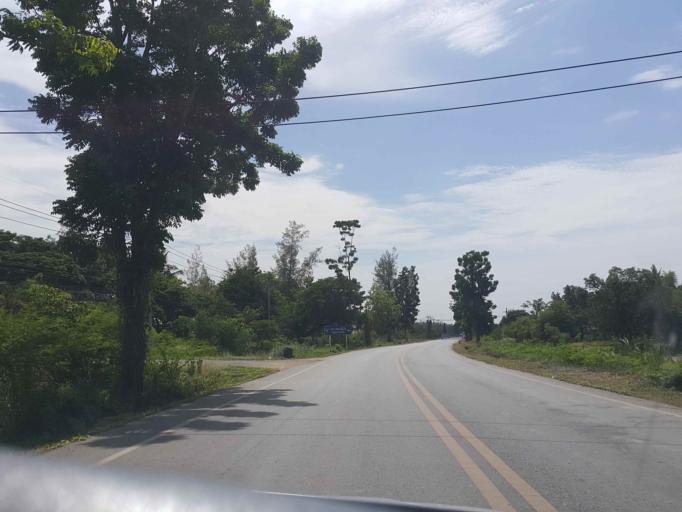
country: TH
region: Sukhothai
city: Thung Saliam
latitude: 17.3304
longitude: 99.5196
